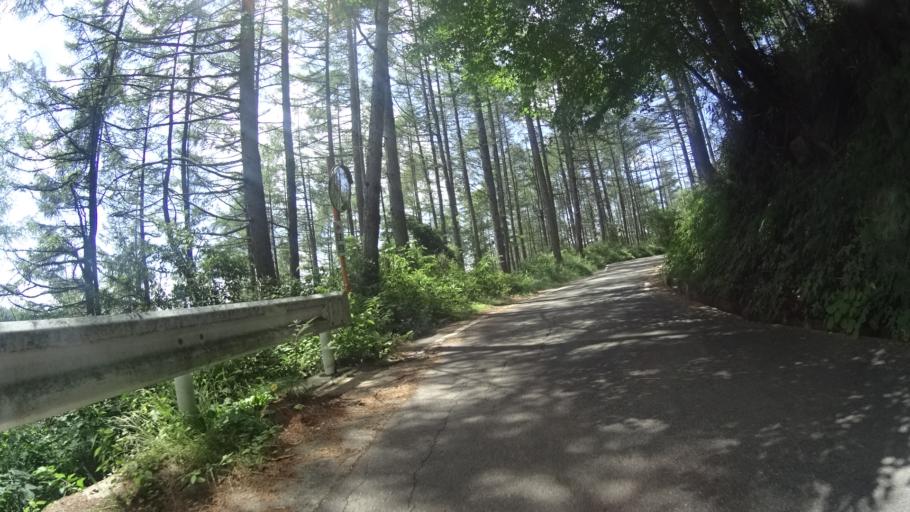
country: JP
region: Yamanashi
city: Enzan
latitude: 35.8366
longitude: 138.6404
